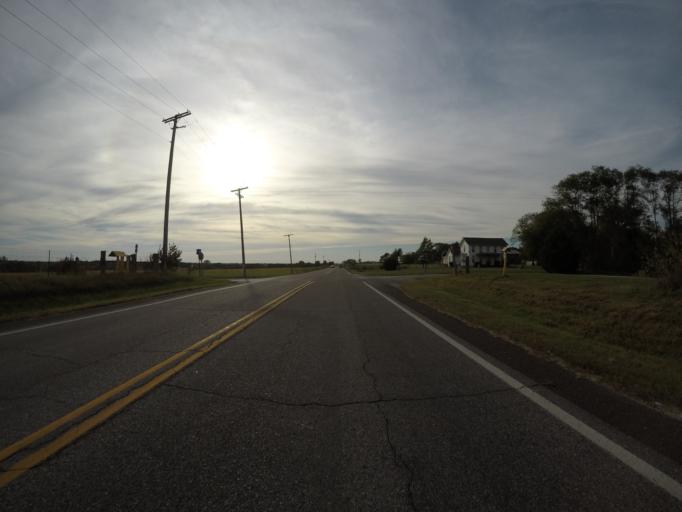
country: US
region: Kansas
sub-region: Douglas County
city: Baldwin City
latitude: 38.7823
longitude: -95.2413
